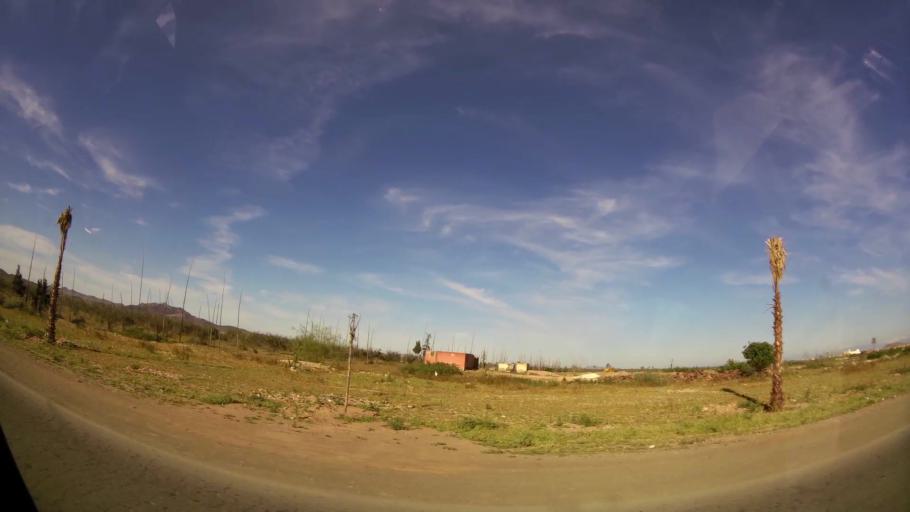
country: MA
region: Marrakech-Tensift-Al Haouz
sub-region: Marrakech
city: Marrakesh
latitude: 31.6881
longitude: -8.0535
